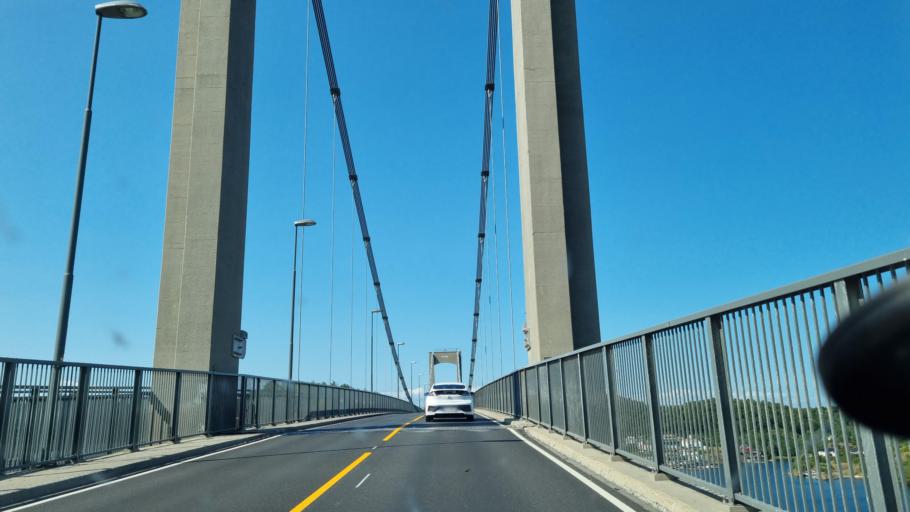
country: NO
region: Aust-Agder
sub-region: Arendal
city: Arendal
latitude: 58.4699
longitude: 8.8236
